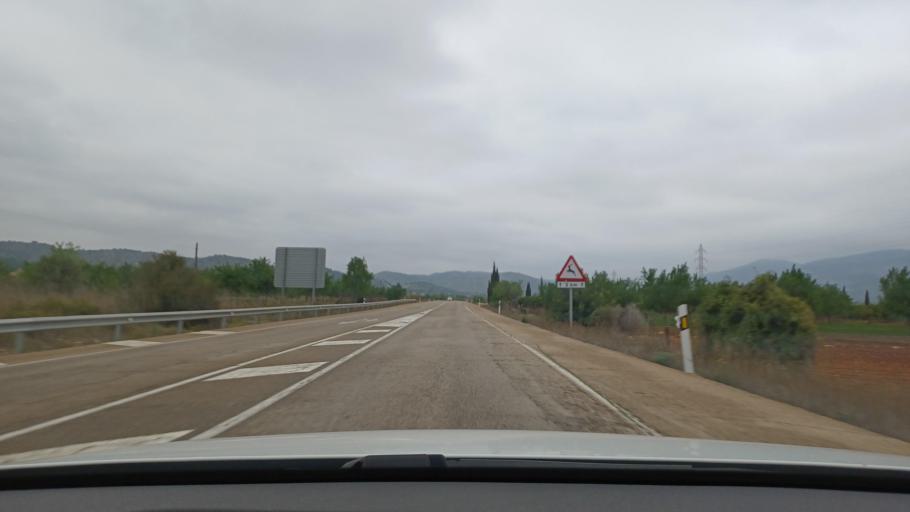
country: ES
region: Valencia
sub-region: Provincia de Castello
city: Torreblanca
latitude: 40.2462
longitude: 0.2325
